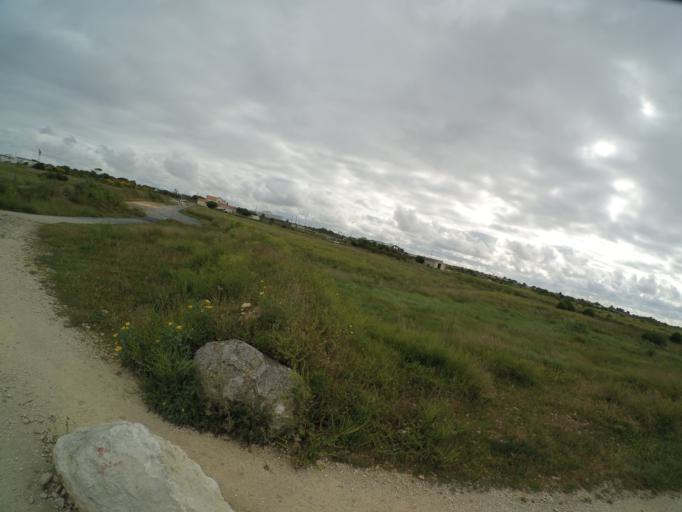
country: FR
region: Poitou-Charentes
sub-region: Departement de la Charente-Maritime
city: La Rochelle
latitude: 46.1332
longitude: -1.1491
